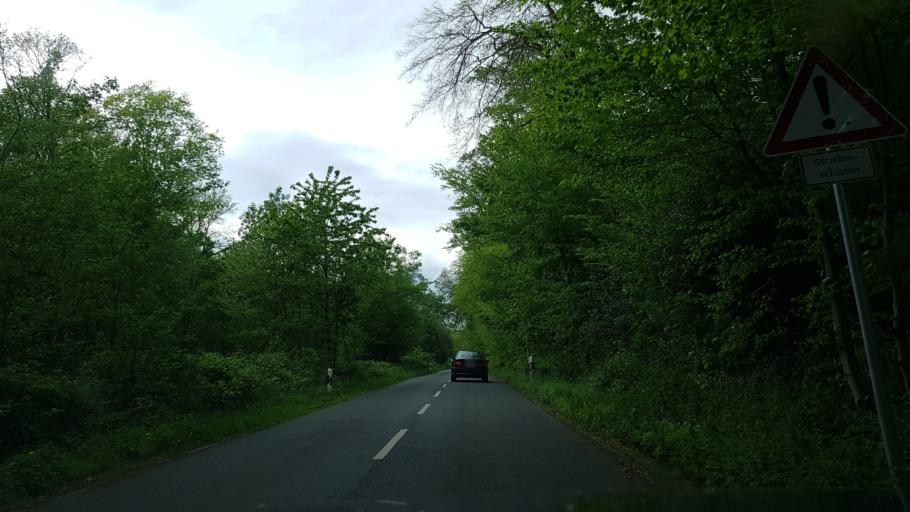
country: DE
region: North Rhine-Westphalia
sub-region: Regierungsbezirk Dusseldorf
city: Muelheim (Ruhr)
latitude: 51.3818
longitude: 6.8497
